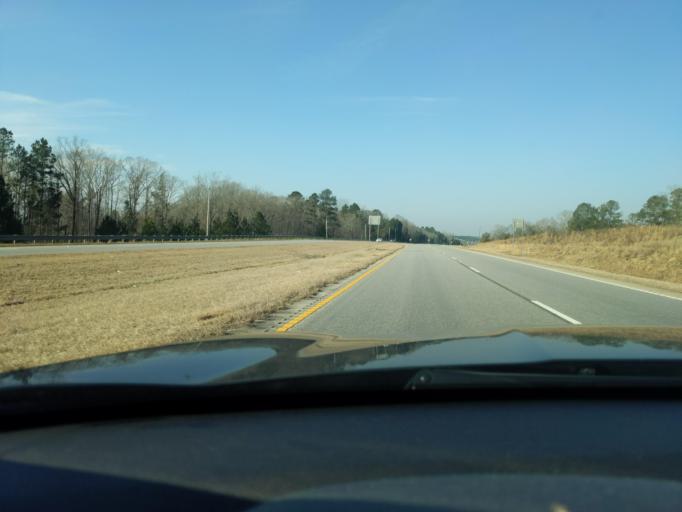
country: US
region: South Carolina
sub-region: Abbeville County
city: Calhoun Falls
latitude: 34.1116
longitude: -82.4926
